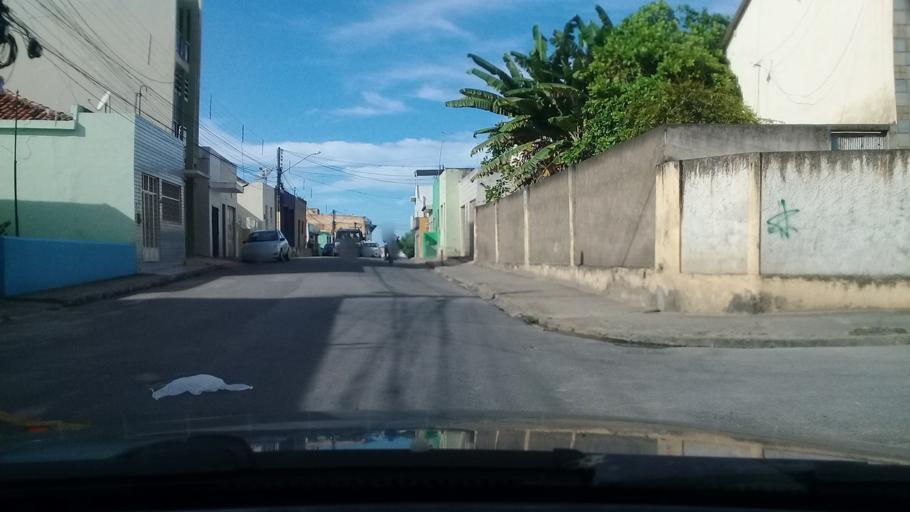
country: BR
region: Pernambuco
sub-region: Vitoria De Santo Antao
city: Vitoria de Santo Antao
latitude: -8.1137
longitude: -35.2916
